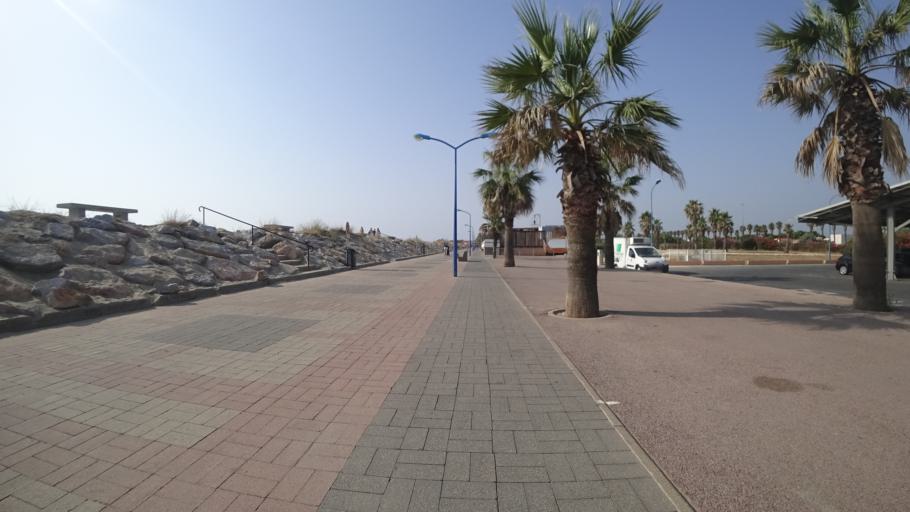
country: FR
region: Languedoc-Roussillon
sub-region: Departement des Pyrenees-Orientales
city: Sainte-Marie-Plage
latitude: 42.7332
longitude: 3.0371
